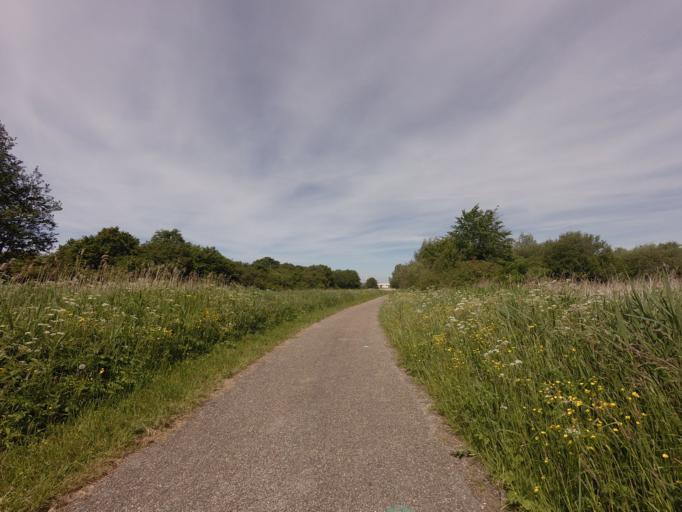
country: NL
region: North Holland
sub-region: Gemeente Zaanstad
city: Zaandam
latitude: 52.3862
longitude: 4.7776
